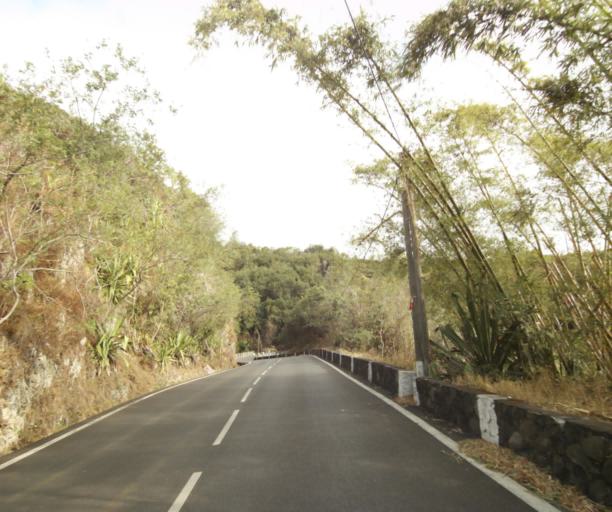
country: RE
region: Reunion
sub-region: Reunion
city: Saint-Paul
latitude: -21.0167
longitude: 55.3183
